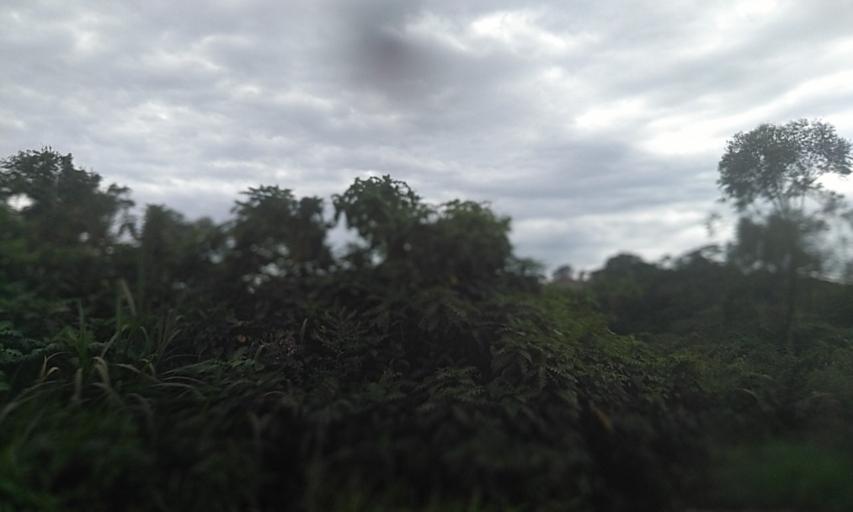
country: UG
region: Central Region
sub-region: Wakiso District
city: Kireka
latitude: 0.4085
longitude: 32.6295
